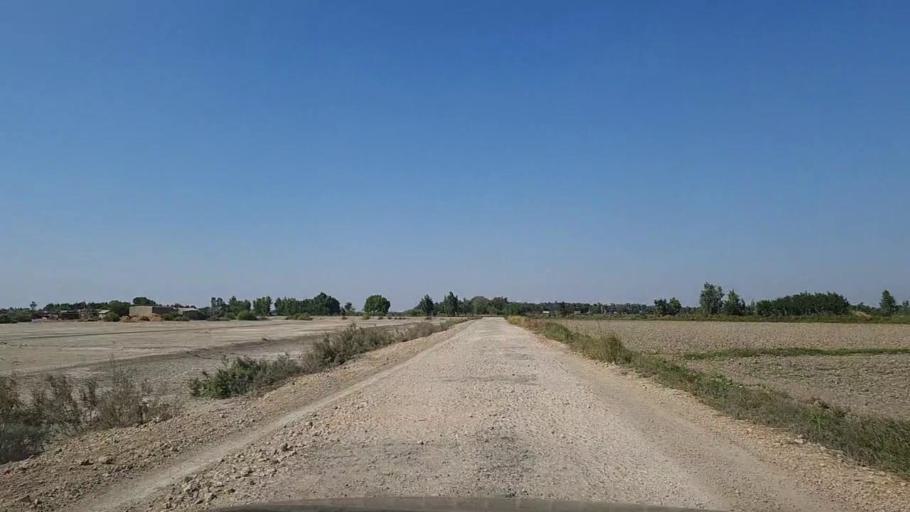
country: PK
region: Sindh
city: Mirpur Sakro
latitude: 24.6109
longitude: 67.7812
